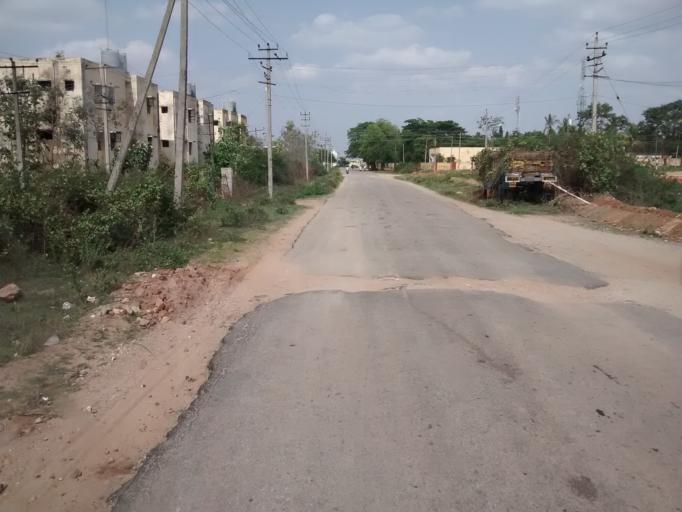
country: IN
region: Karnataka
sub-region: Mysore
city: Hunsur
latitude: 12.3364
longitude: 76.4480
